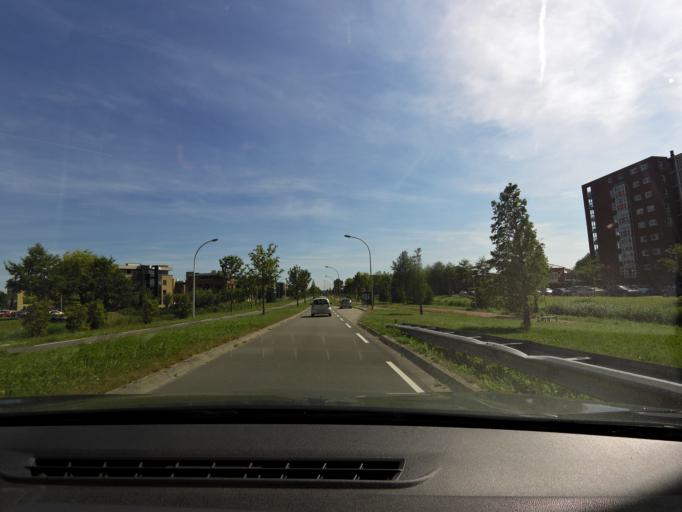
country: NL
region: South Holland
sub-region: Gemeente Barendrecht
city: Barendrecht
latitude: 51.8538
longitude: 4.5086
